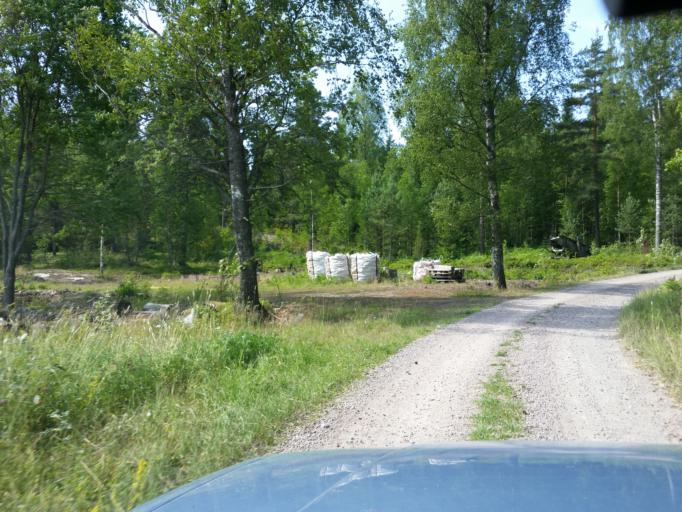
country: FI
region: Varsinais-Suomi
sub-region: Aboland-Turunmaa
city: Nagu
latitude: 60.2046
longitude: 22.0911
